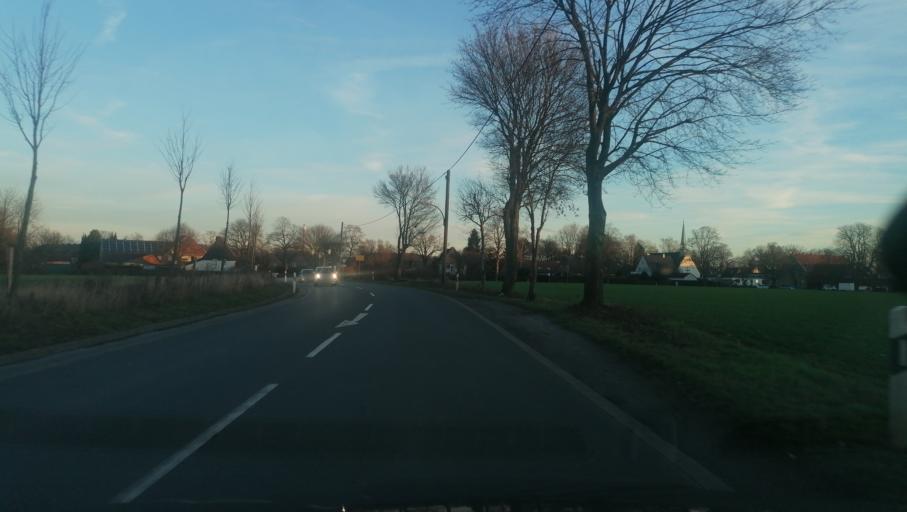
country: DE
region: North Rhine-Westphalia
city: Bergkamen
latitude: 51.6006
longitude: 7.6155
